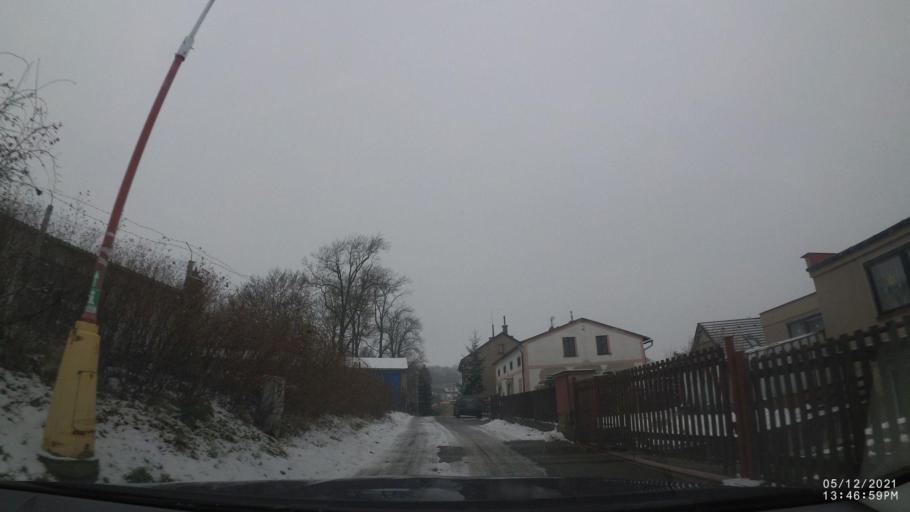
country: CZ
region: Kralovehradecky
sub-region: Okres Nachod
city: Police nad Metuji
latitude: 50.5351
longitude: 16.2353
